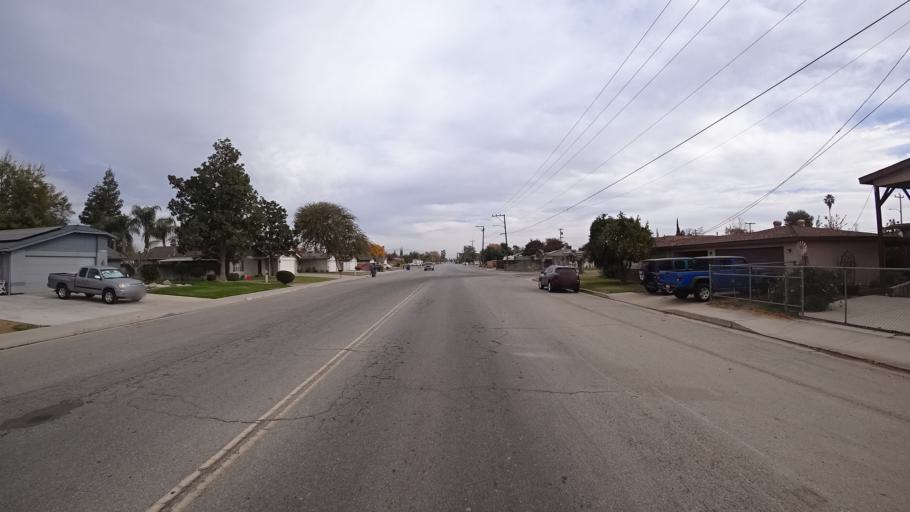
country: US
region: California
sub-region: Kern County
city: Greenacres
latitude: 35.3907
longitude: -119.1244
